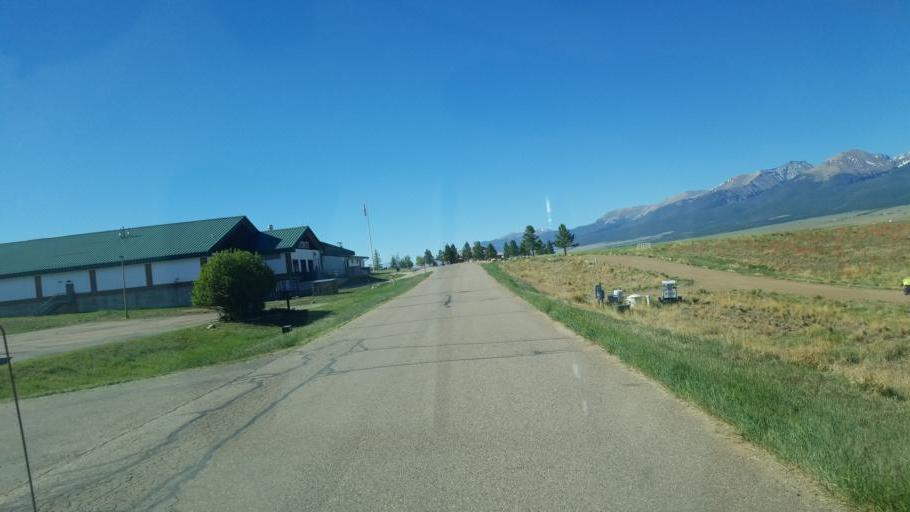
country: US
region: Colorado
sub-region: Custer County
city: Westcliffe
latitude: 38.1376
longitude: -105.4730
